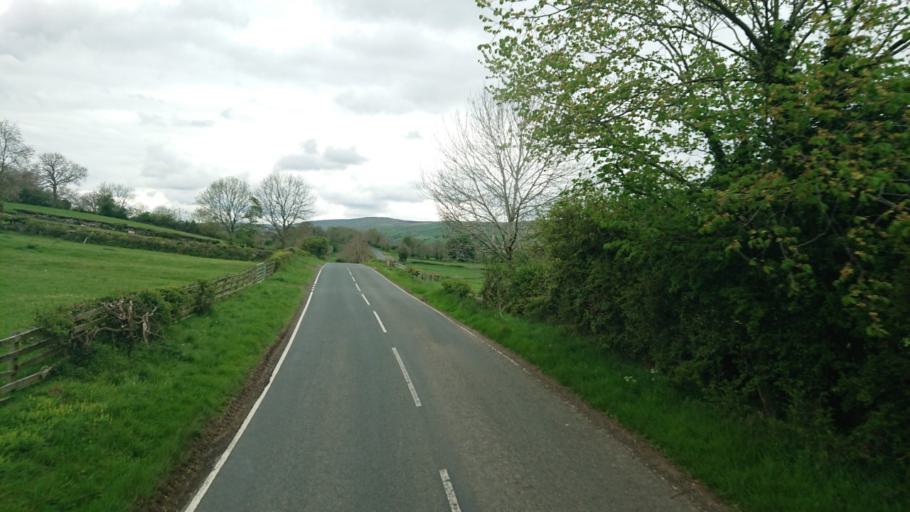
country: GB
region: England
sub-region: North Yorkshire
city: Leyburn
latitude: 54.2762
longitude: -1.9828
